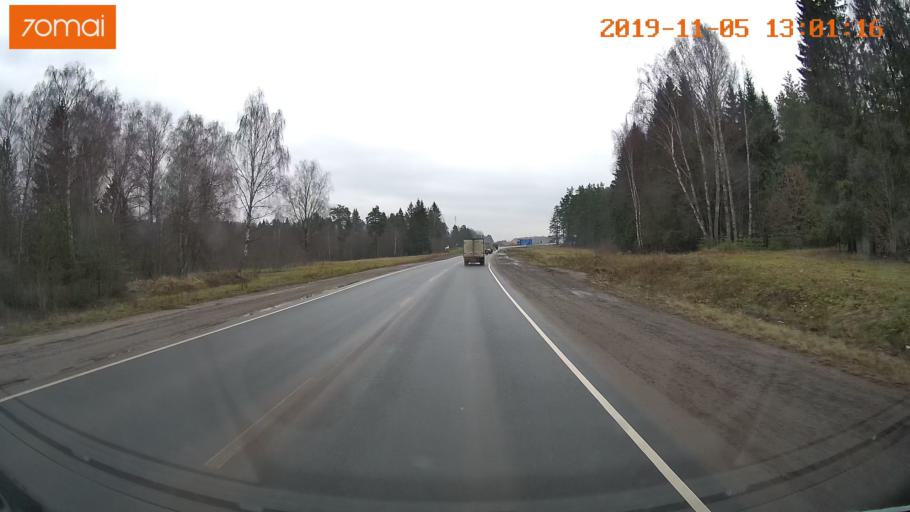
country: RU
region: Ivanovo
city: Kokhma
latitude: 56.9099
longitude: 41.1591
